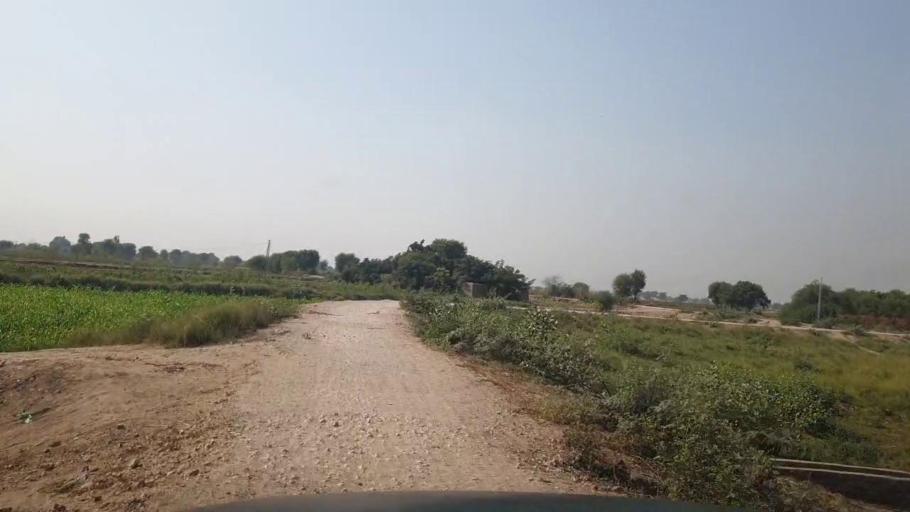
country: PK
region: Sindh
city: Bhit Shah
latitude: 25.7391
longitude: 68.5005
